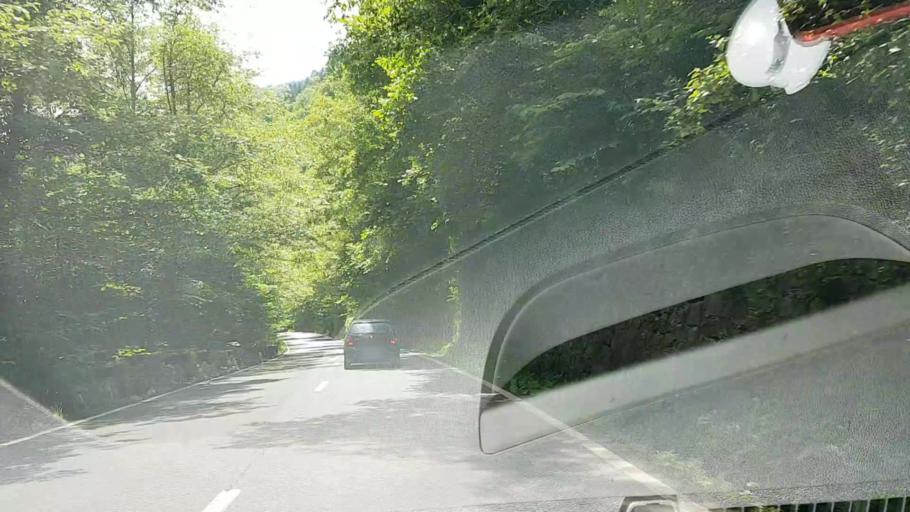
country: RO
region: Suceava
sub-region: Comuna Crucea
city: Crucea
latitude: 47.2946
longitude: 25.6319
